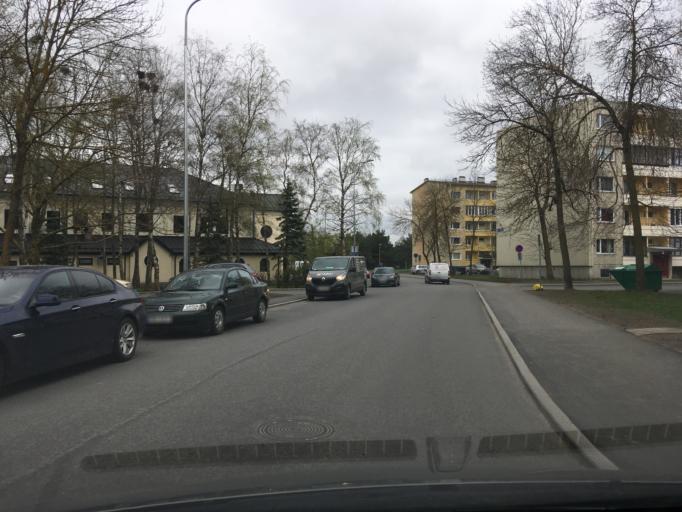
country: EE
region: Harju
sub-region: Tallinna linn
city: Kose
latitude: 59.4370
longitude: 24.8361
